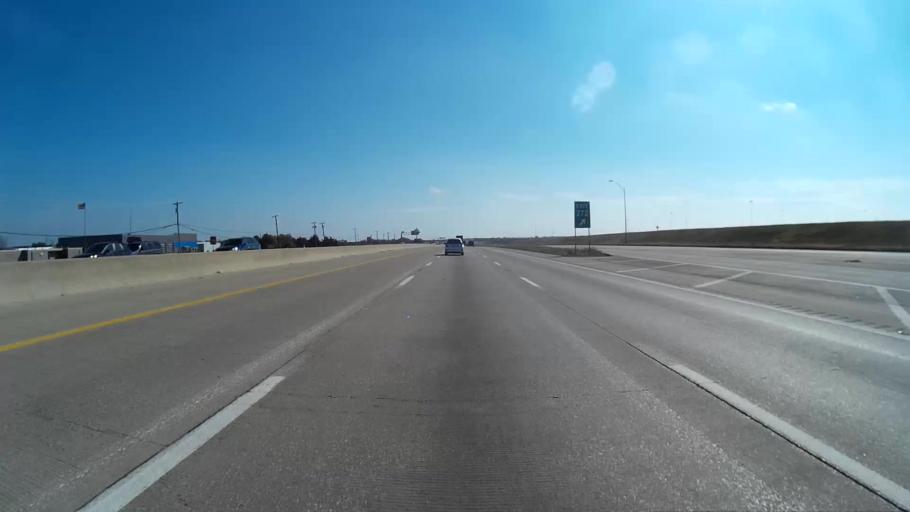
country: US
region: Texas
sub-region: Dallas County
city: Hutchins
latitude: 32.6307
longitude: -96.6986
